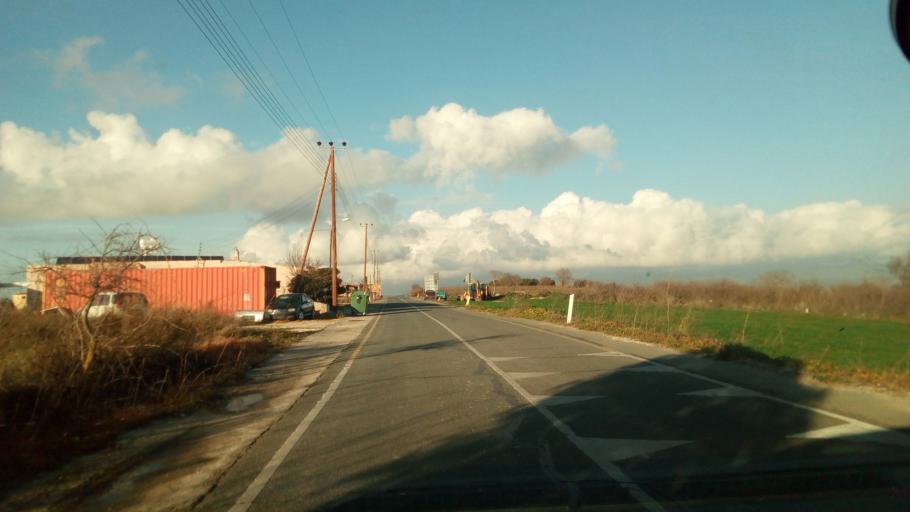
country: CY
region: Pafos
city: Mesogi
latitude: 34.8518
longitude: 32.4945
